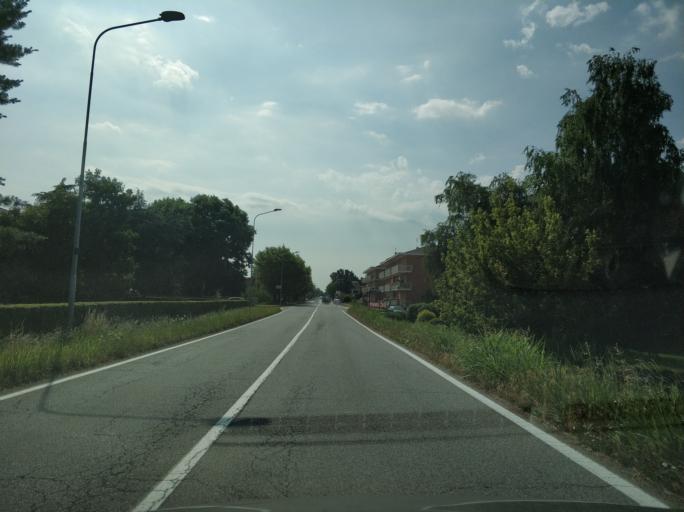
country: IT
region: Piedmont
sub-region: Provincia di Torino
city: Poirino
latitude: 44.9171
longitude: 7.8407
